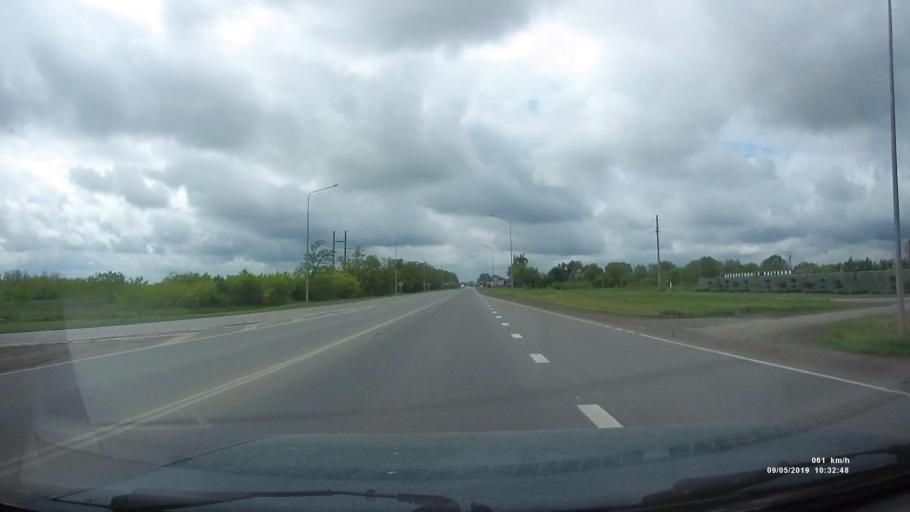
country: RU
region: Rostov
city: Azov
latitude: 47.0691
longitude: 39.4257
